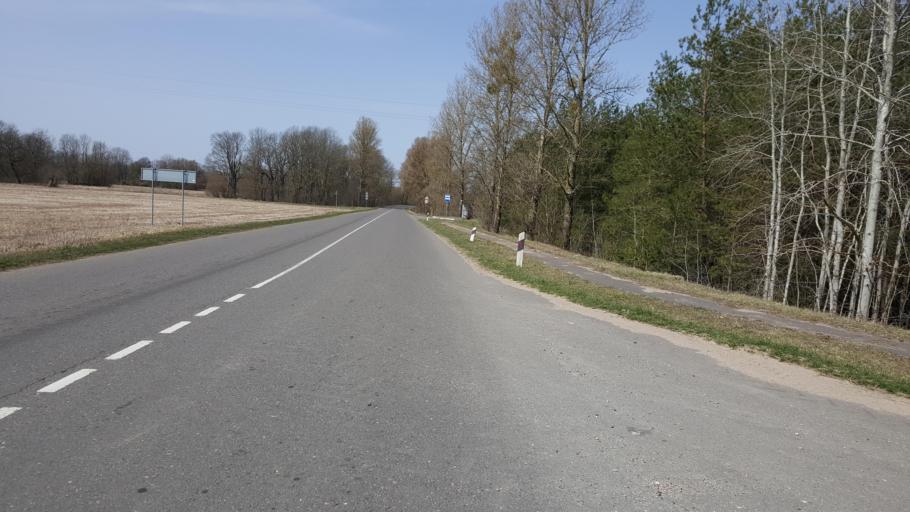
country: BY
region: Brest
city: Kamyanyuki
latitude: 52.4904
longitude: 23.6887
